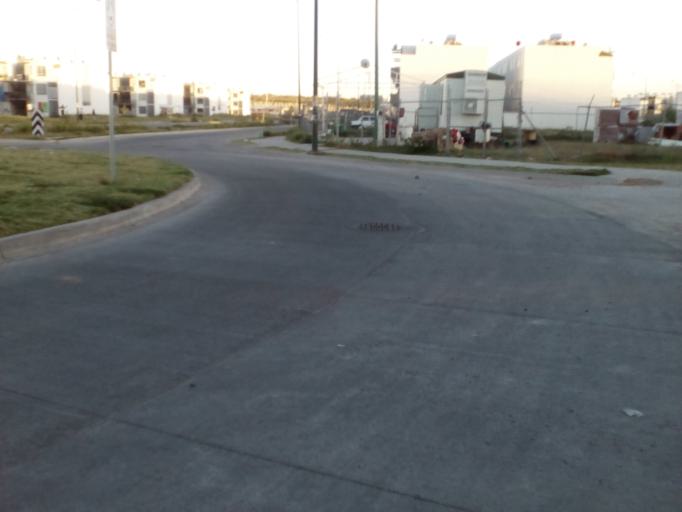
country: MX
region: Guanajuato
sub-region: Leon
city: Fraccionamiento Paseo de las Torres
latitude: 21.1854
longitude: -101.7680
